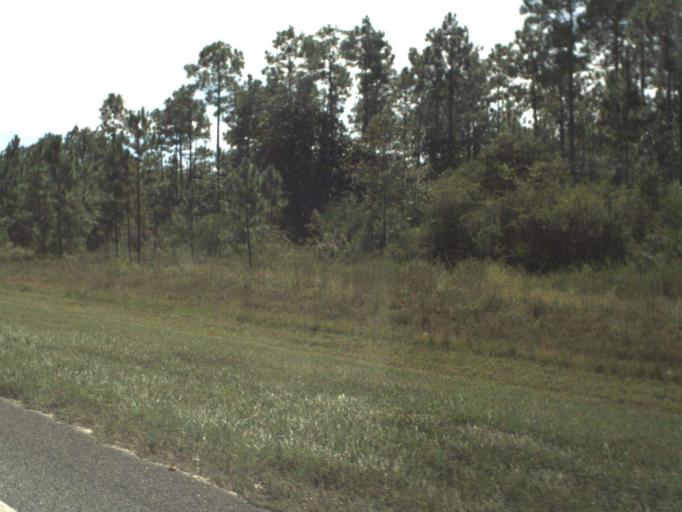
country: US
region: Florida
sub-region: Bay County
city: Lynn Haven
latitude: 30.3686
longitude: -85.6743
